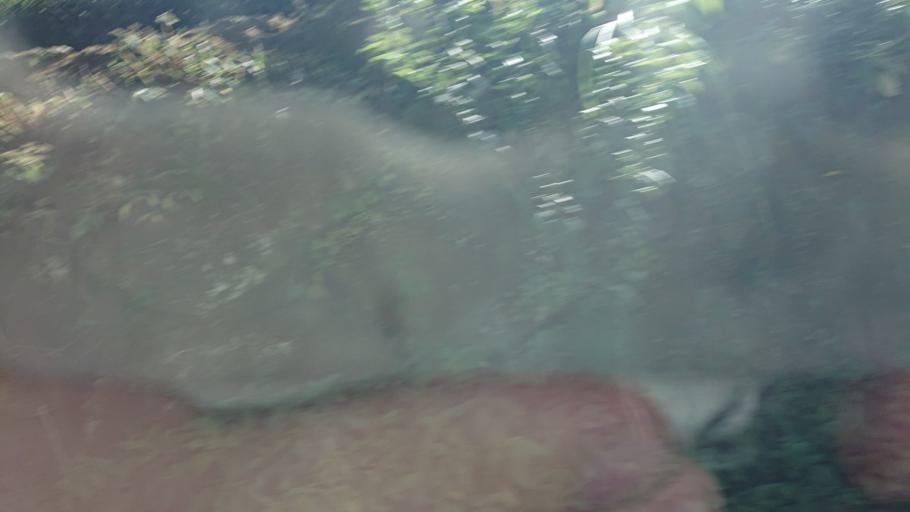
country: TW
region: Taiwan
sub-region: Chiayi
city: Jiayi Shi
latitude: 23.4768
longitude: 120.6984
